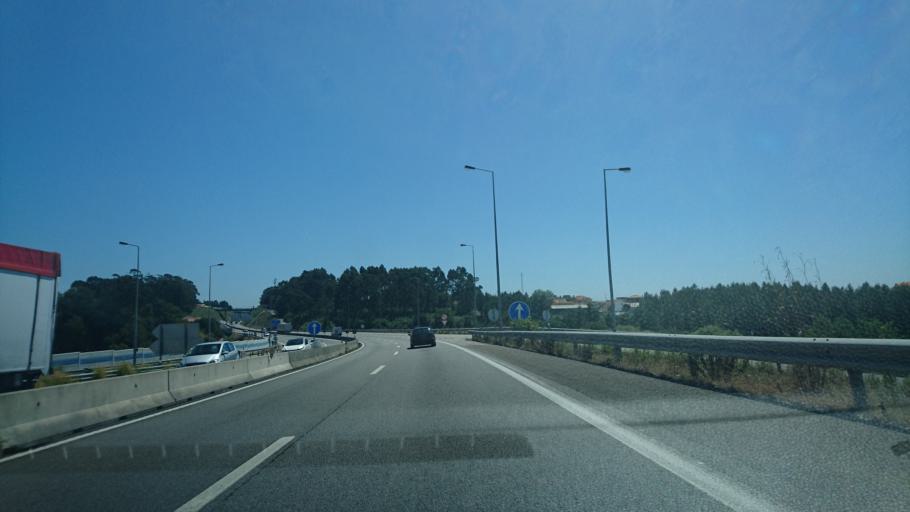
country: PT
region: Porto
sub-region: Vila Nova de Gaia
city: Vila Nova da Telha
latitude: 41.0634
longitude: -8.6418
